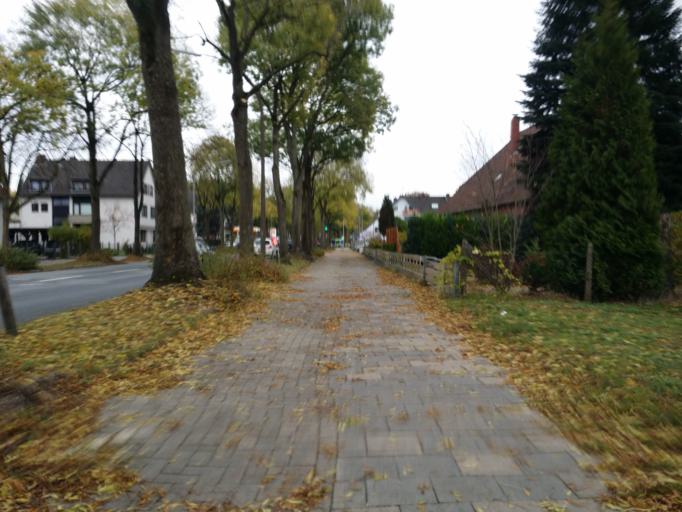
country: DE
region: Lower Saxony
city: Delmenhorst
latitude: 53.0455
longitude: 8.6682
